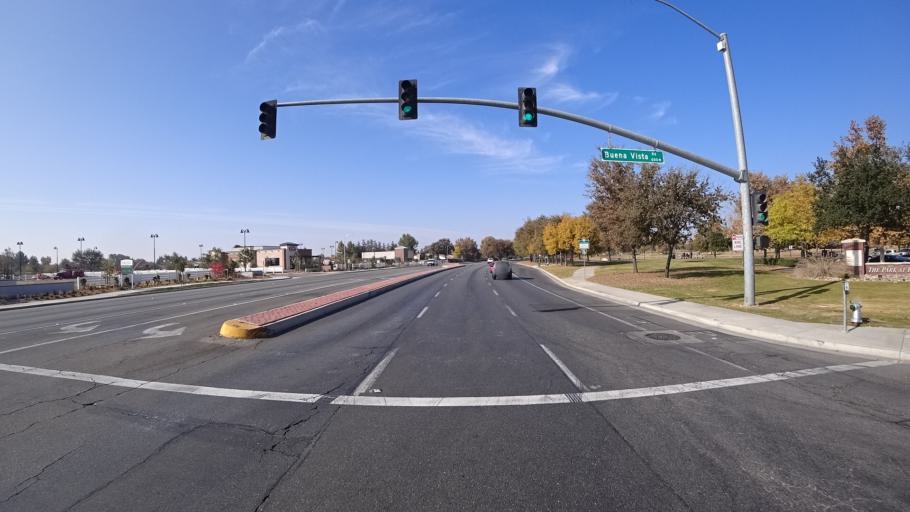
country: US
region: California
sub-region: Kern County
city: Greenacres
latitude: 35.3490
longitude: -119.1273
